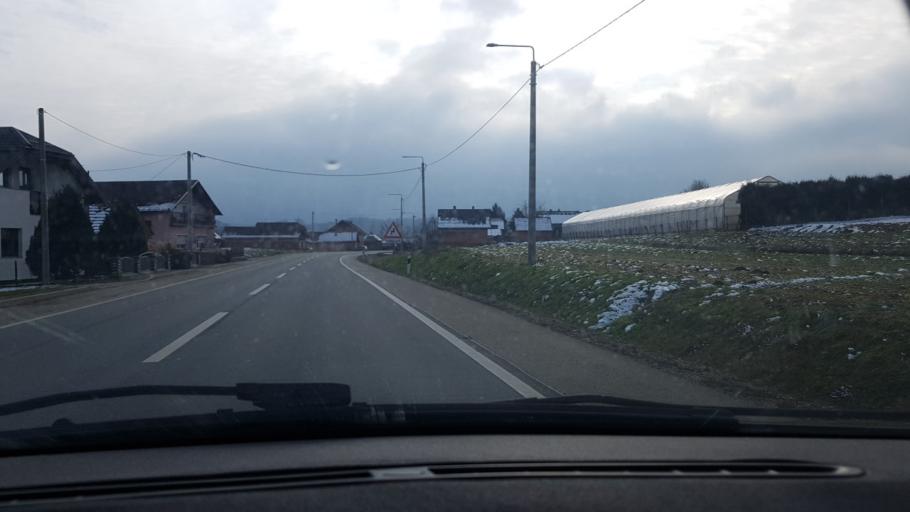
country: HR
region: Varazdinska
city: Tuzno
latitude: 46.2671
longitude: 16.2093
